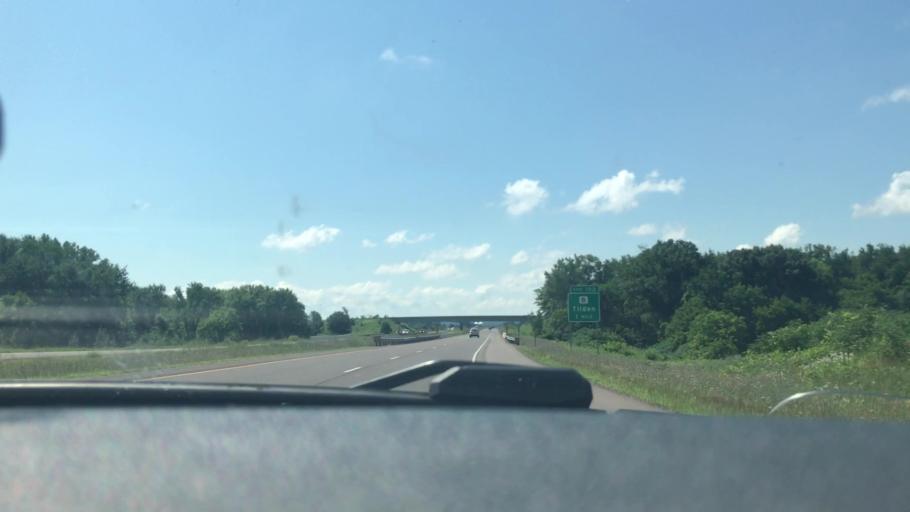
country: US
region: Wisconsin
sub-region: Chippewa County
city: Bloomer
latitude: 45.0196
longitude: -91.4432
